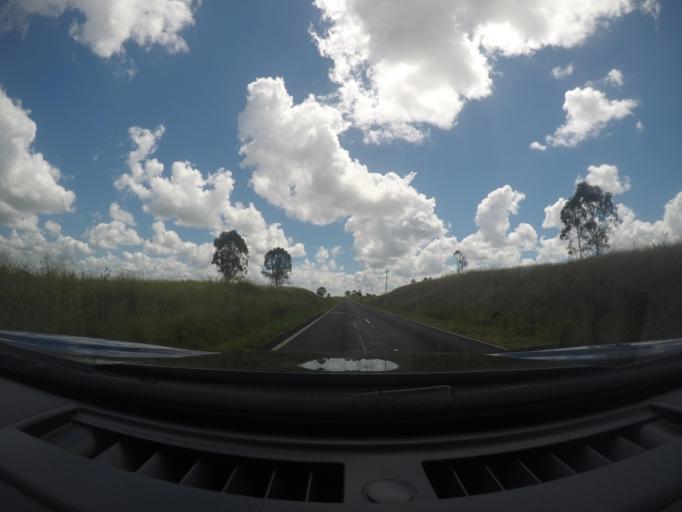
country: AU
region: Queensland
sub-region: Moreton Bay
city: Woodford
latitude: -27.1399
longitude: 152.5030
